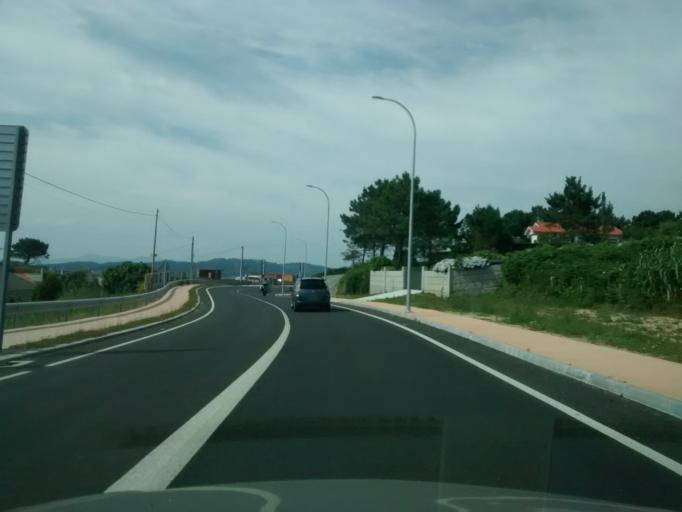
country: ES
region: Galicia
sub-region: Provincia de Pontevedra
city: Sanxenxo
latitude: 42.4232
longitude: -8.8742
